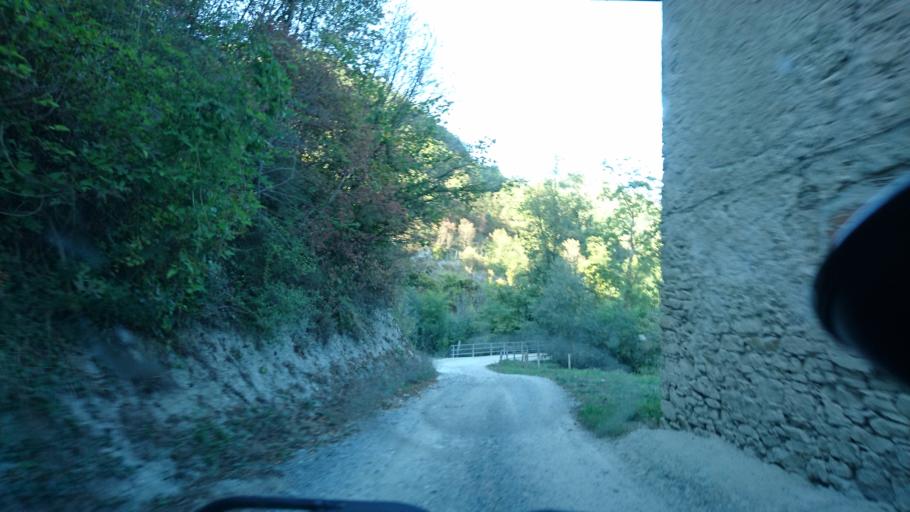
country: IT
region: Piedmont
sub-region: Provincia di Asti
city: Bubbio
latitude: 44.6705
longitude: 8.3035
